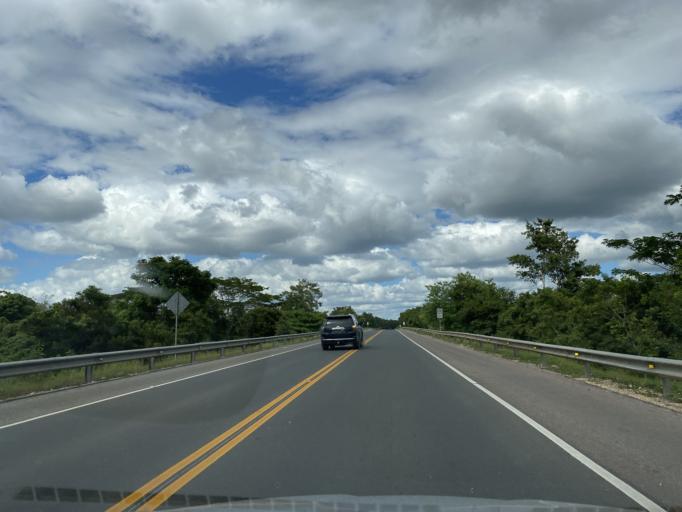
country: DO
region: Santo Domingo
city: Guerra
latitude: 18.5882
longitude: -69.7697
